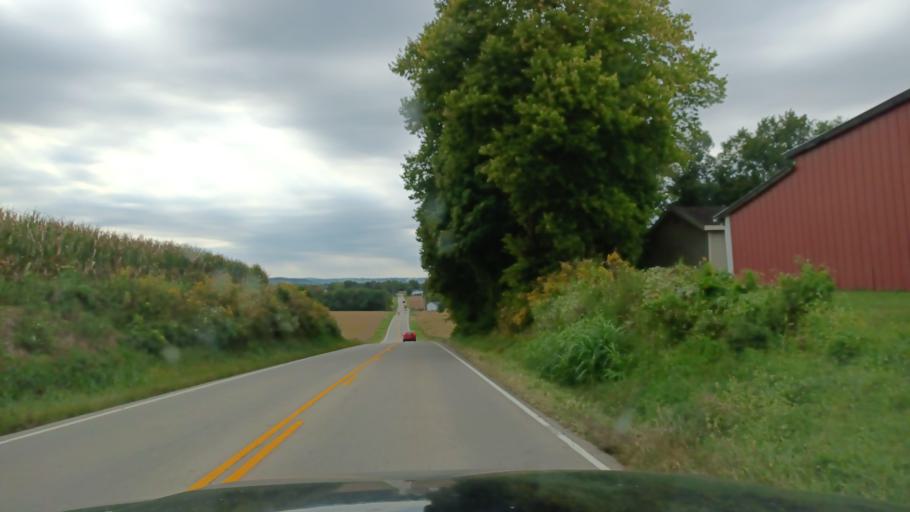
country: US
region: Ohio
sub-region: Ross County
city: Chillicothe
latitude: 39.2941
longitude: -82.8873
